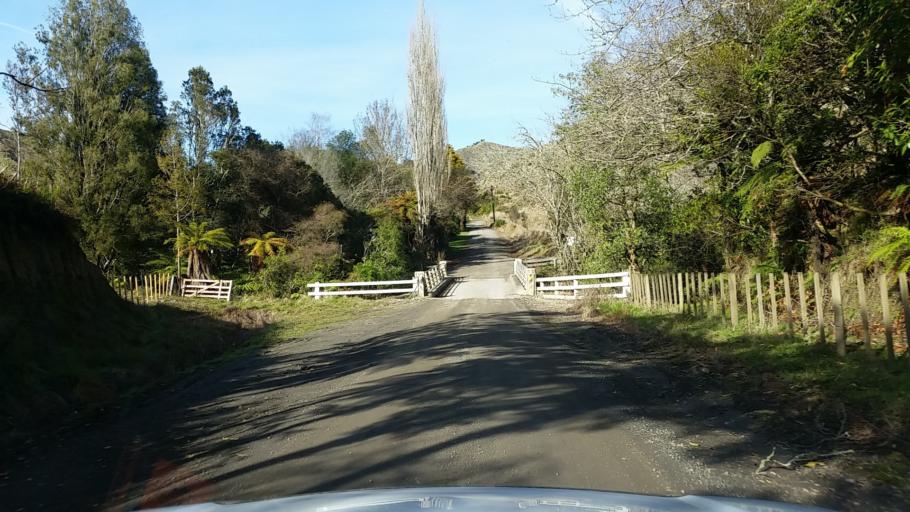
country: NZ
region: Taranaki
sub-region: South Taranaki District
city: Eltham
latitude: -39.3587
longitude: 174.5124
